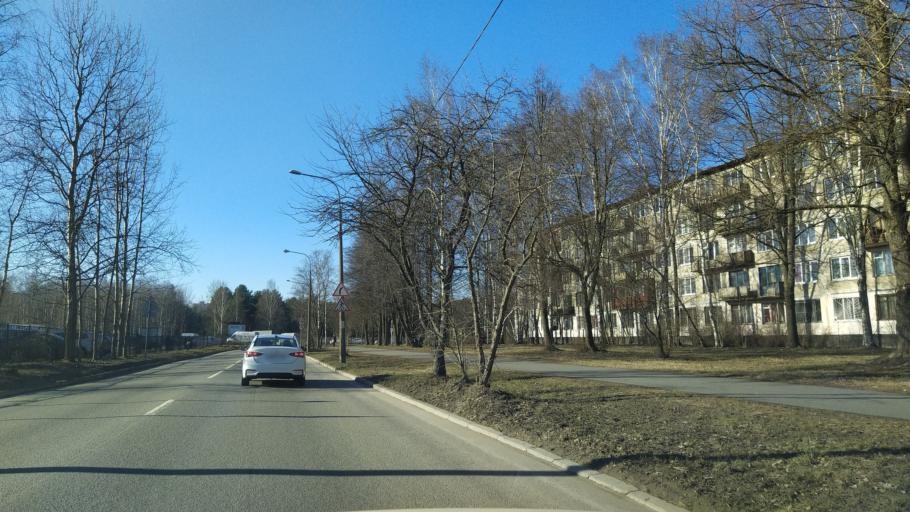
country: RU
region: Leningrad
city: Akademicheskoe
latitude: 60.0007
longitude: 30.4239
